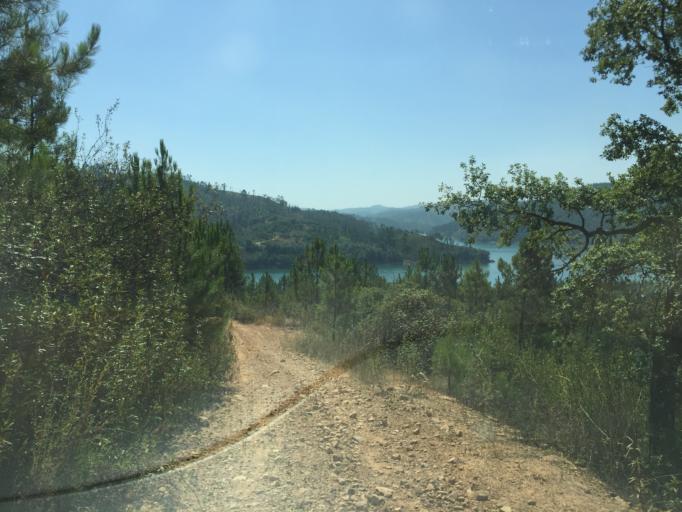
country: PT
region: Santarem
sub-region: Ferreira do Zezere
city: Ferreira do Zezere
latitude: 39.6523
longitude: -8.2387
